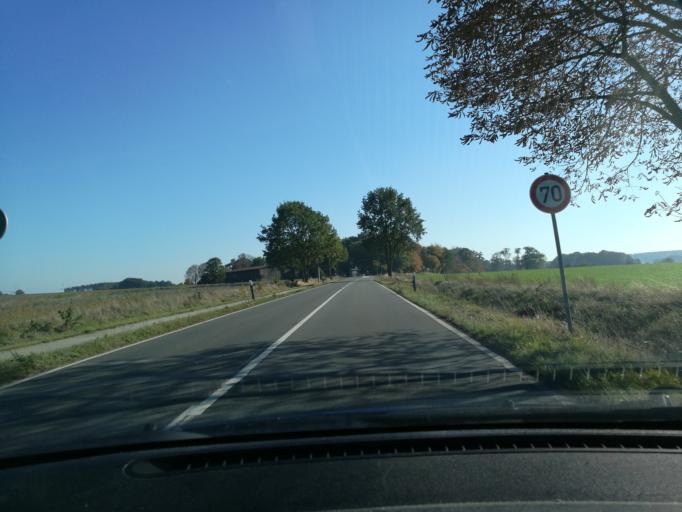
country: DE
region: Lower Saxony
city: Wendisch Evern
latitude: 53.2268
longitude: 10.4546
